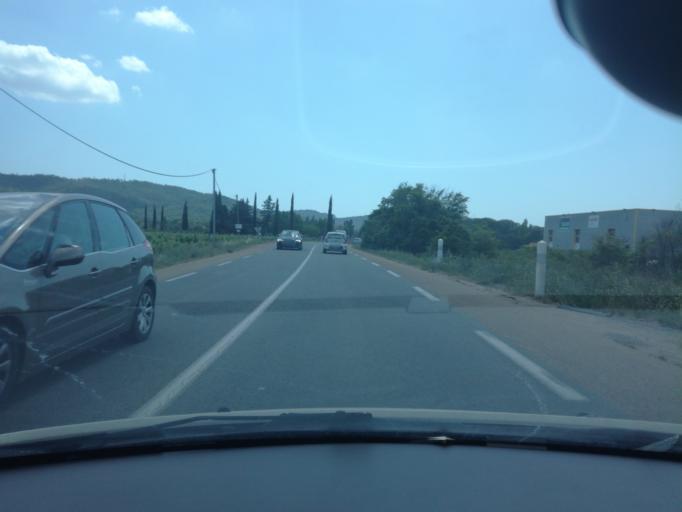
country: FR
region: Provence-Alpes-Cote d'Azur
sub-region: Departement du Var
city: Les Arcs
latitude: 43.4492
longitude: 6.4872
